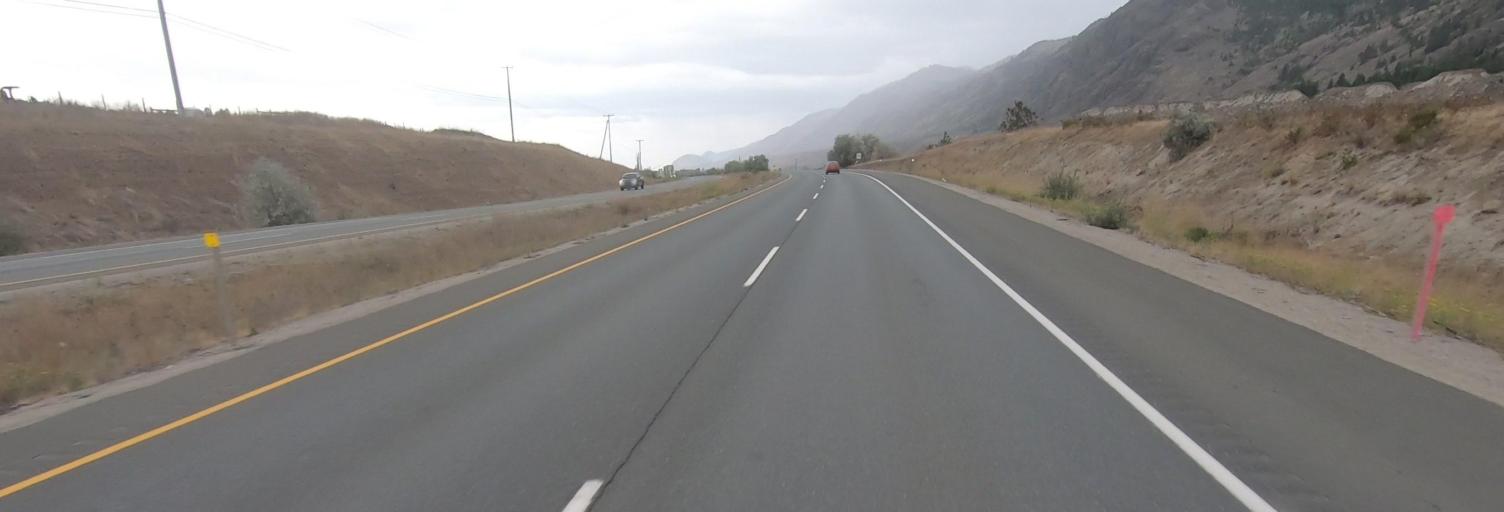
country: CA
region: British Columbia
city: Chase
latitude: 50.6457
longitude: -119.9233
